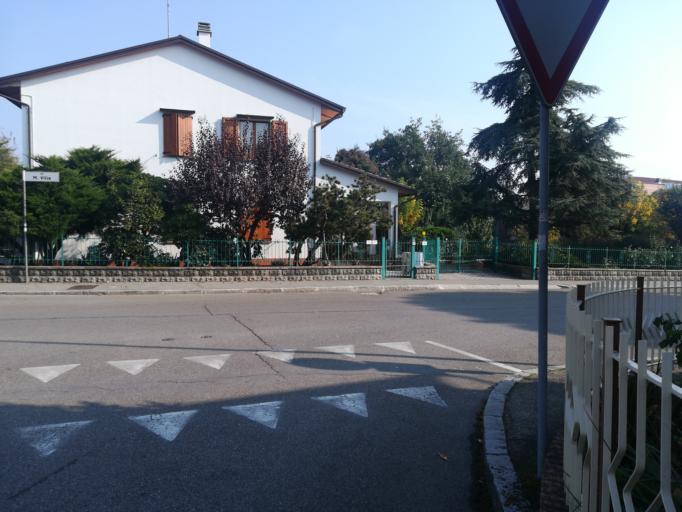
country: IT
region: Emilia-Romagna
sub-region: Provincia di Bologna
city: Imola
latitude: 44.3639
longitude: 11.6923
